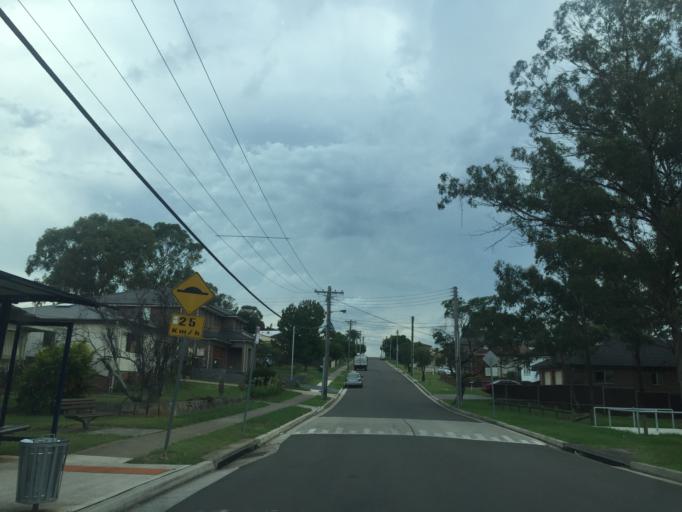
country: AU
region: New South Wales
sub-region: Blacktown
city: Blacktown
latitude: -33.7850
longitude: 150.8993
